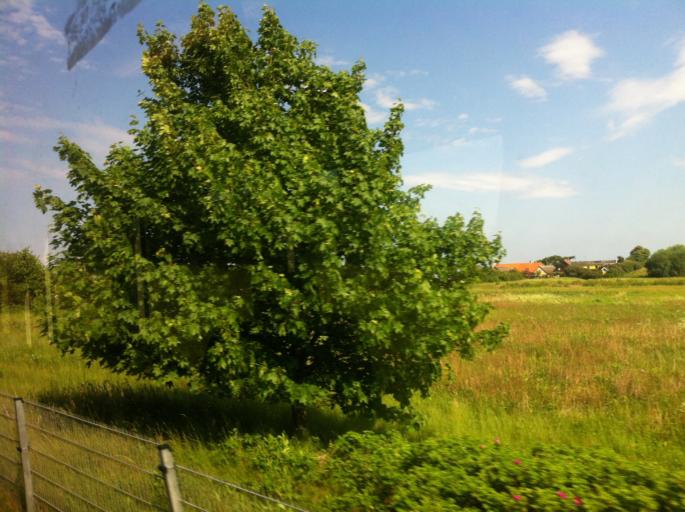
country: DK
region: Capital Region
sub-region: Helsingor Kommune
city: Hornbaek
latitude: 56.0962
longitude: 12.3998
